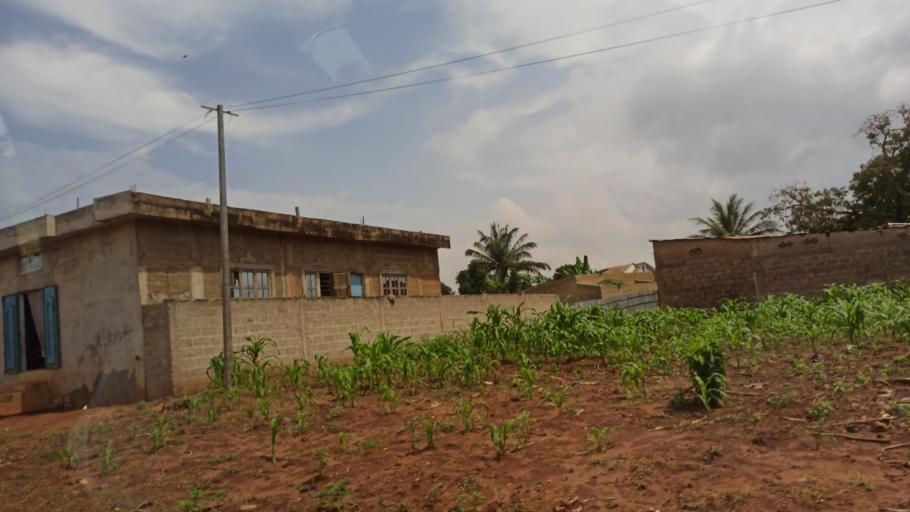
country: BJ
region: Queme
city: Porto-Novo
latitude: 6.4855
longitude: 2.5904
